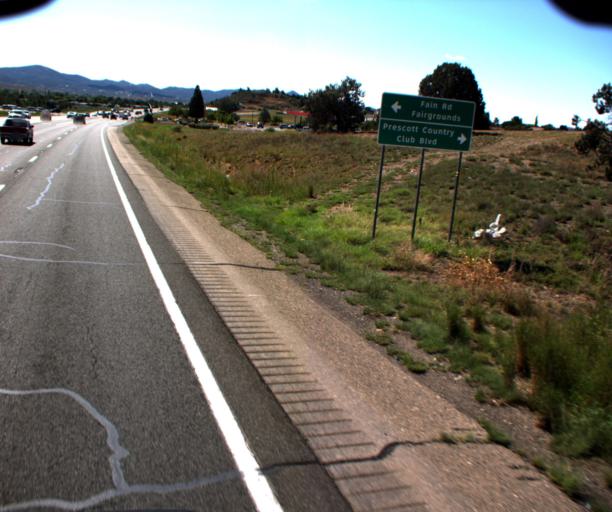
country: US
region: Arizona
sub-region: Yavapai County
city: Dewey-Humboldt
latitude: 34.5634
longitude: -112.2618
